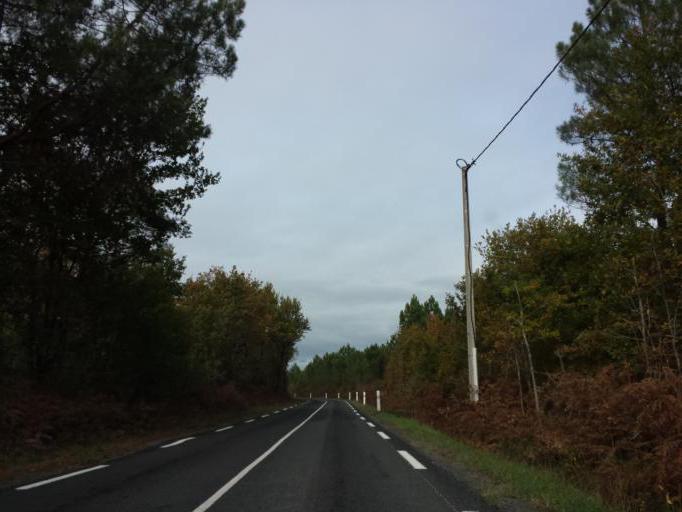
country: FR
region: Aquitaine
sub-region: Departement de la Gironde
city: Lacanau
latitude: 44.9455
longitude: -1.0650
